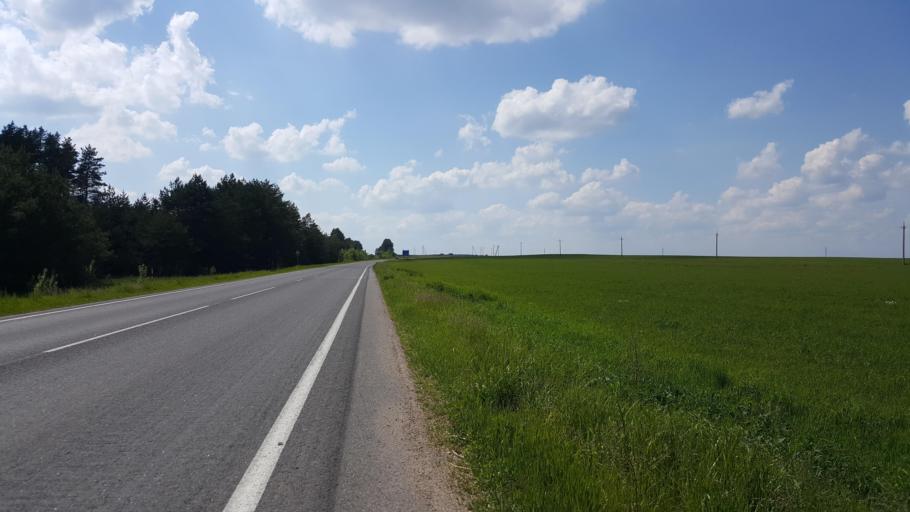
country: BY
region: Brest
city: Kamyanyets
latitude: 52.4010
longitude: 23.8763
